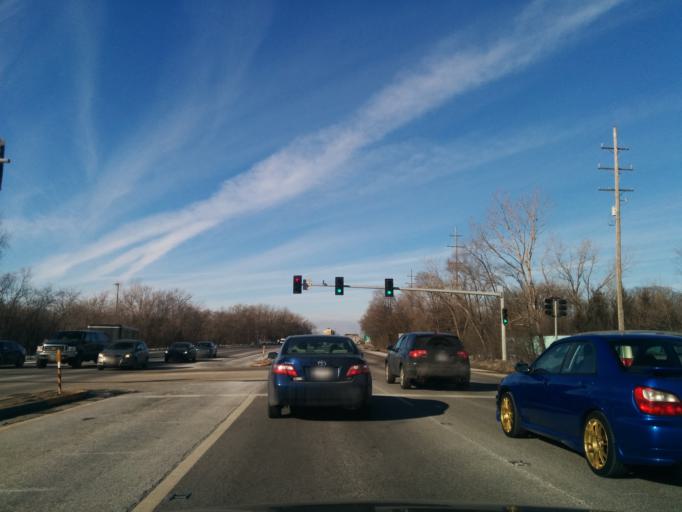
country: US
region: Illinois
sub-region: DuPage County
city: Elmhurst
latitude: 41.8995
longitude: -87.9643
